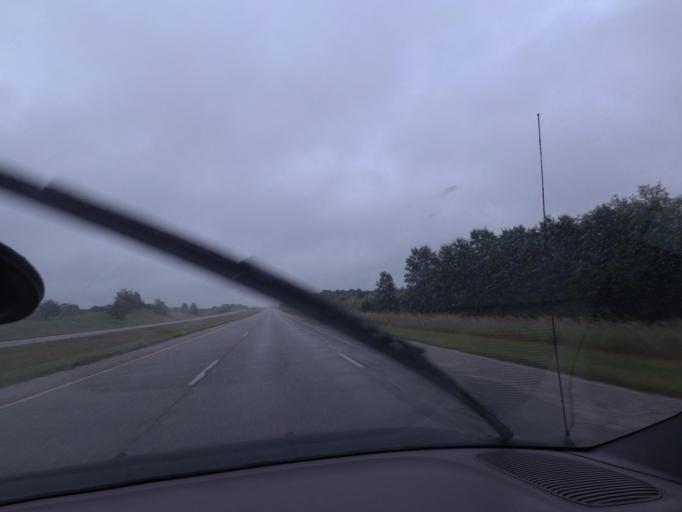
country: US
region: Illinois
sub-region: Pike County
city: Barry
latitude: 39.6927
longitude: -90.9687
